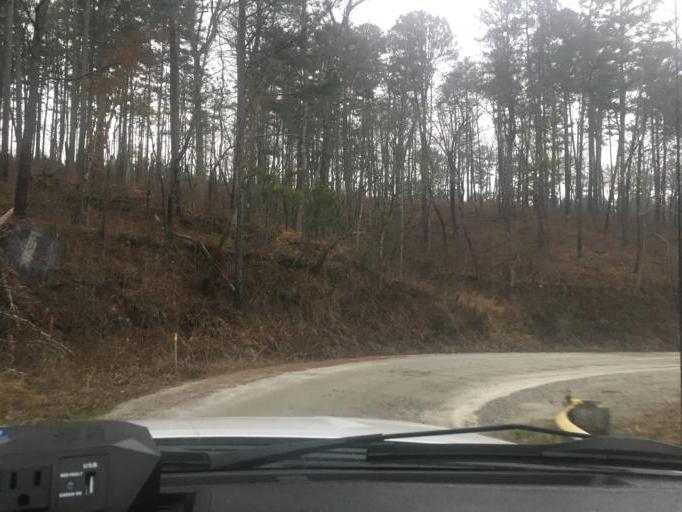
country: US
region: Georgia
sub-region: Dawson County
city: Dawsonville
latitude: 34.4452
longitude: -84.2090
